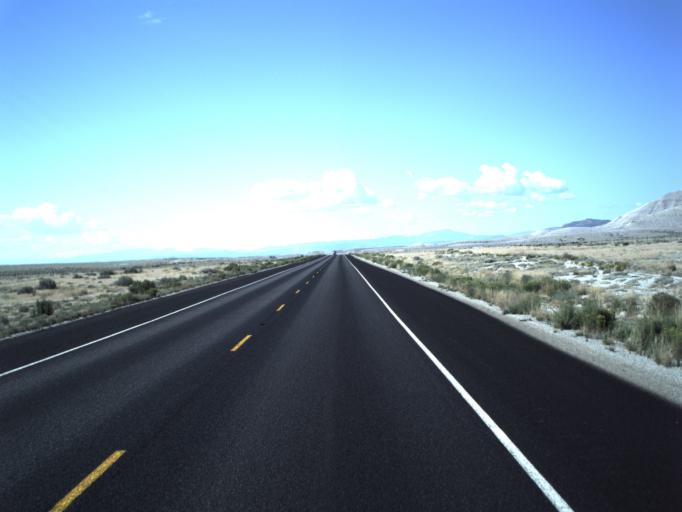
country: US
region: Utah
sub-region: Emery County
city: Ferron
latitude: 39.0085
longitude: -111.1530
